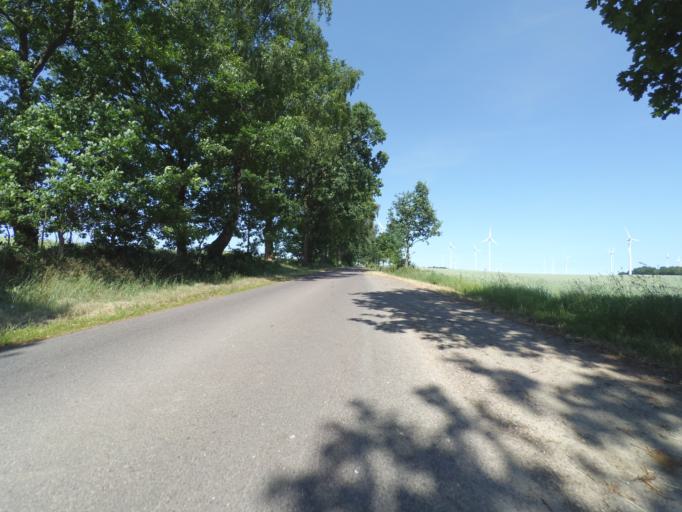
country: DE
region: Brandenburg
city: Gerdshagen
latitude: 53.2487
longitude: 12.3050
